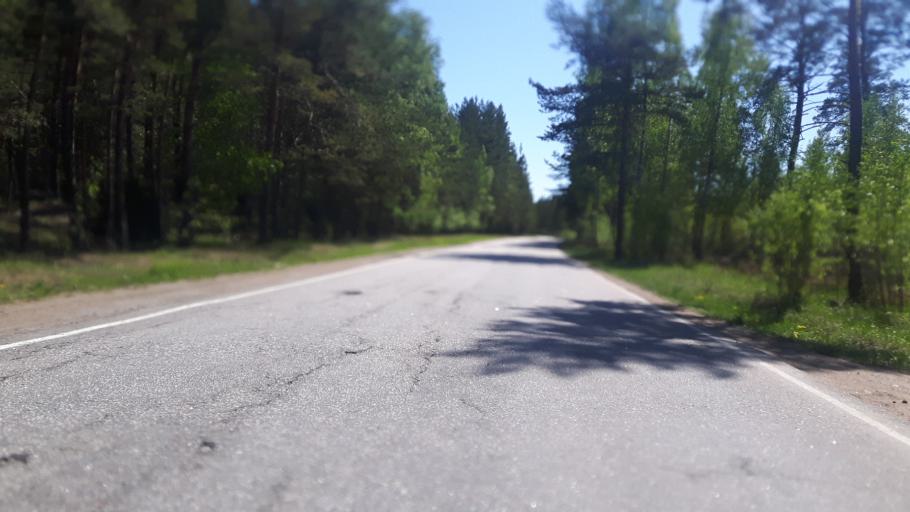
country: RU
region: Leningrad
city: Glebychevo
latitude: 60.3502
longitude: 28.8173
